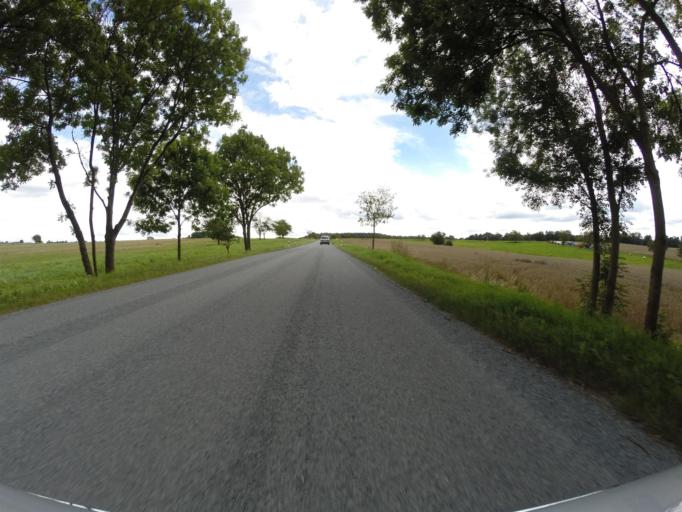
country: DE
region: Thuringia
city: Schongleina
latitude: 50.9072
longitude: 11.7300
